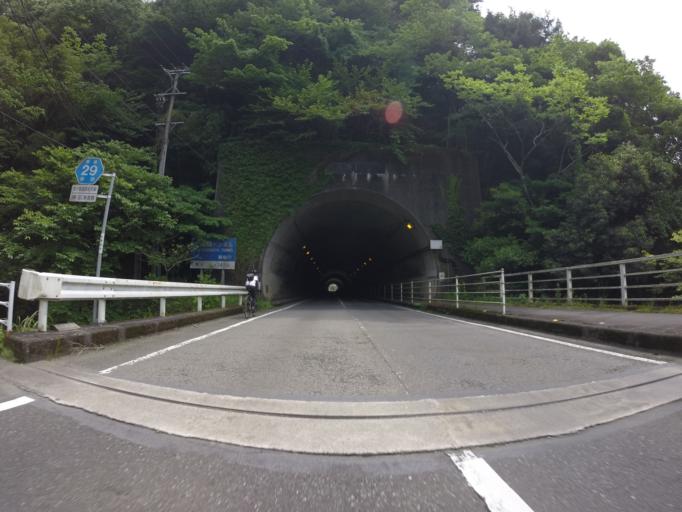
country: JP
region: Shizuoka
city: Shizuoka-shi
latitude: 35.0886
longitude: 138.3760
